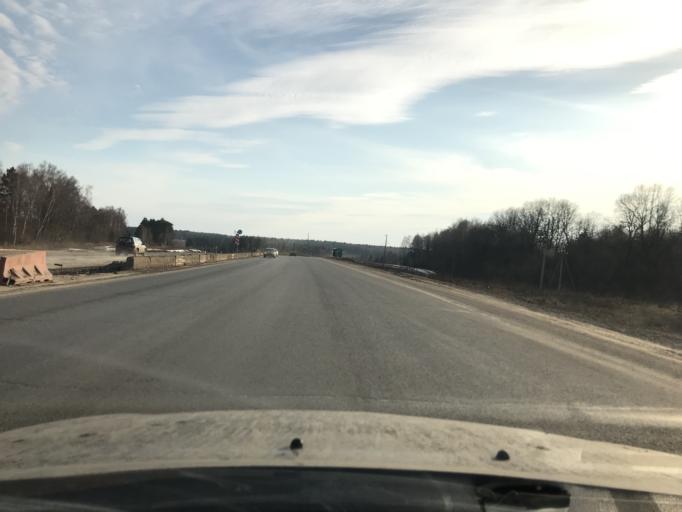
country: RU
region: Kaluga
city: Kaluga
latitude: 54.4313
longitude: 36.2119
